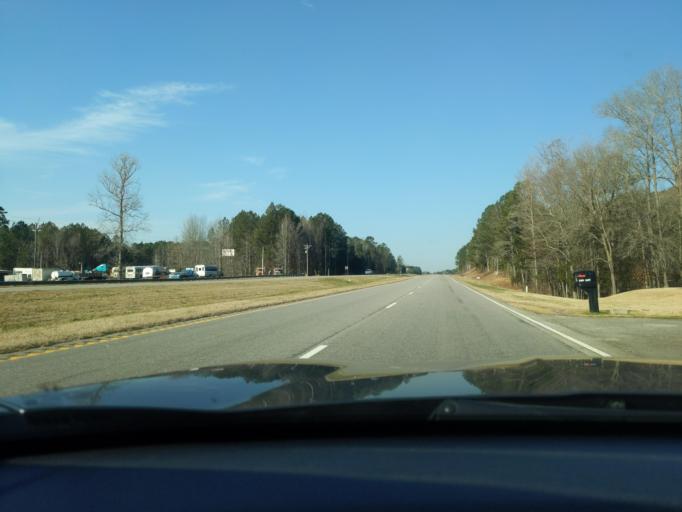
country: US
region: South Carolina
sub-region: Greenwood County
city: Greenwood
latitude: 34.1897
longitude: -82.2584
